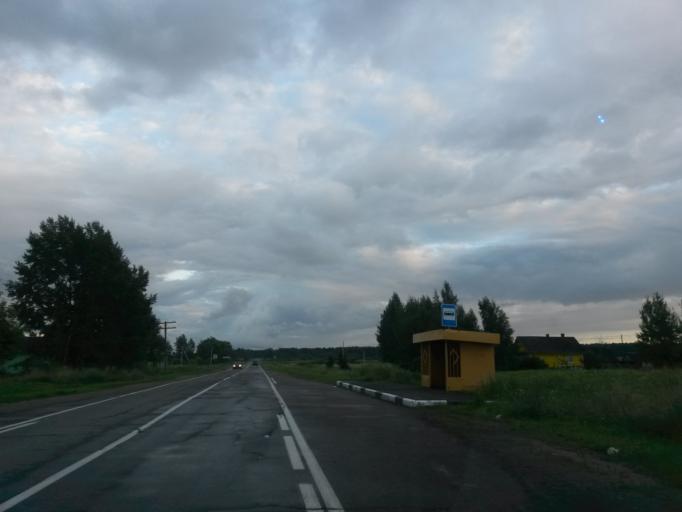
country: RU
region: Jaroslavl
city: Tutayev
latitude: 57.9378
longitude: 39.4995
